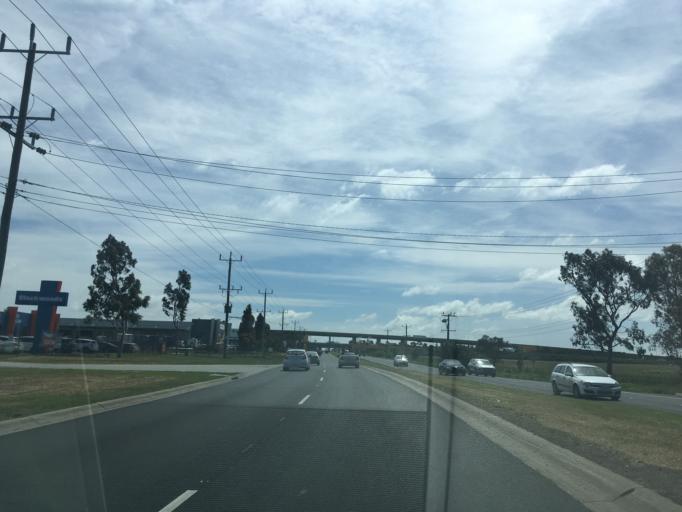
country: AU
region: Victoria
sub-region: Brimbank
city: Derrimut
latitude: -37.8049
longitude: 144.7884
